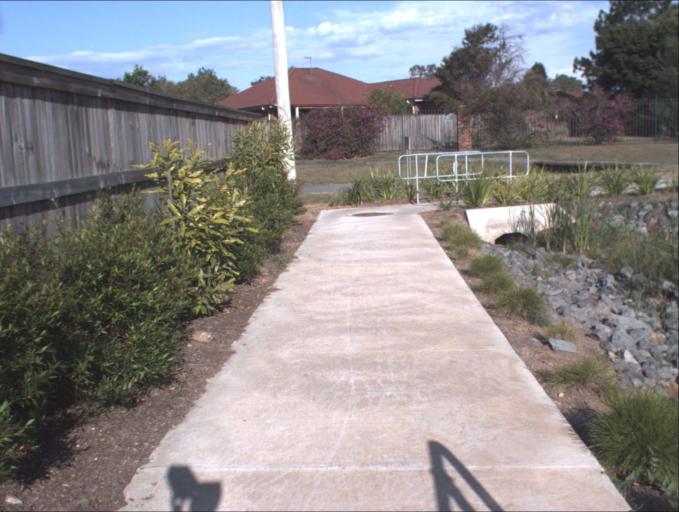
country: AU
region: Queensland
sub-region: Logan
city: Beenleigh
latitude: -27.6730
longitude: 153.2062
